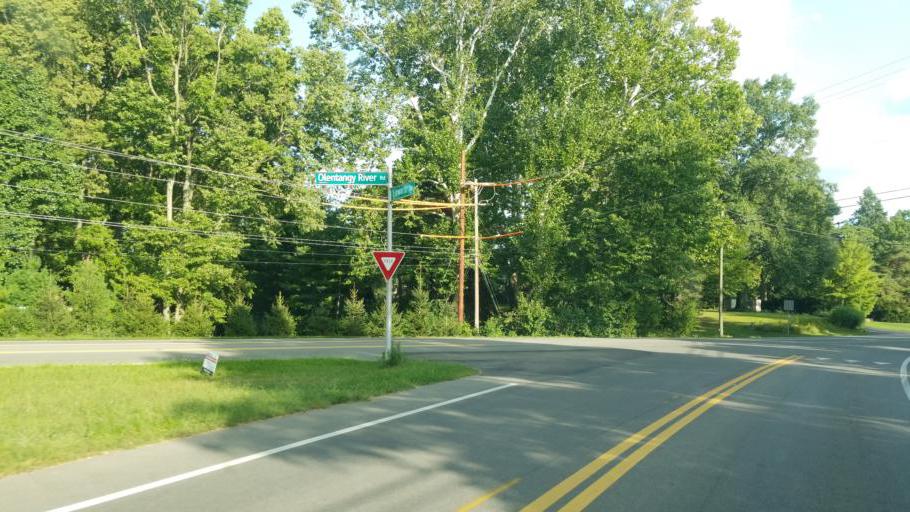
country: US
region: Ohio
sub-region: Franklin County
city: Worthington
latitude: 40.0675
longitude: -83.0402
